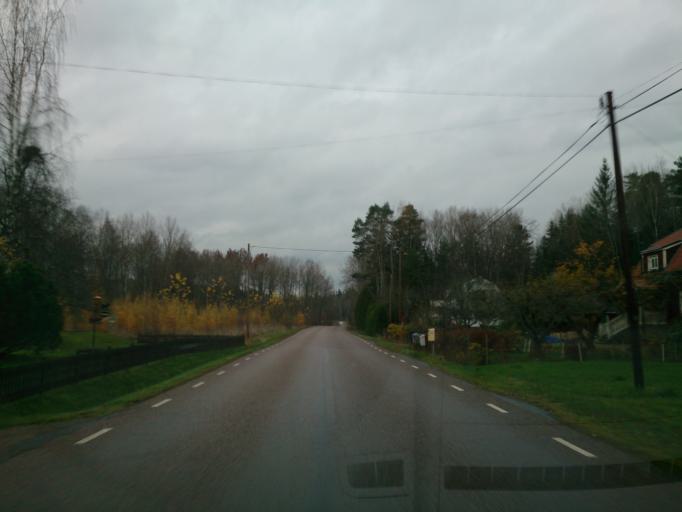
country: SE
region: OEstergoetland
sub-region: Atvidabergs Kommun
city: Atvidaberg
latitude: 58.3118
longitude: 16.0246
